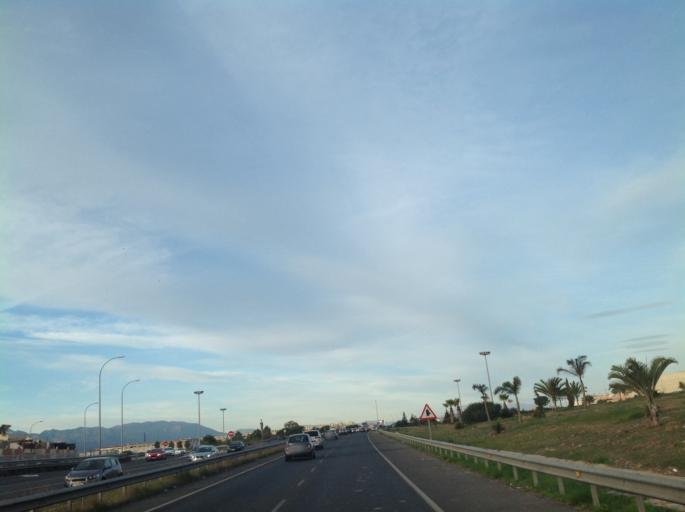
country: ES
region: Andalusia
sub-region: Provincia de Malaga
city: Malaga
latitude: 36.7138
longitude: -4.4544
